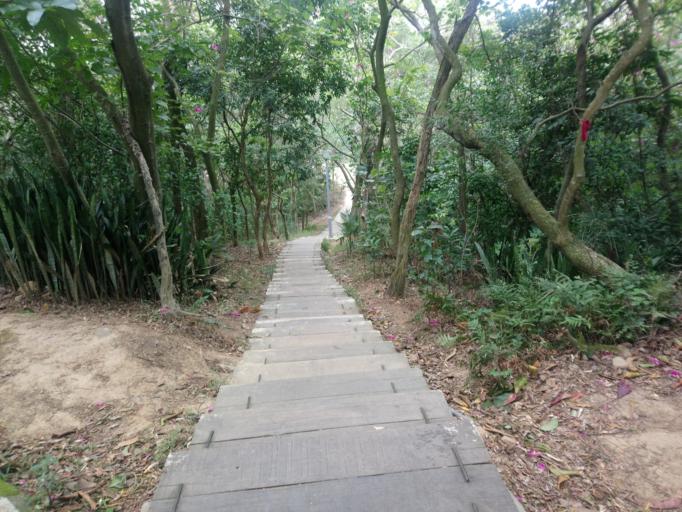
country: TW
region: Taiwan
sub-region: Hsinchu
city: Hsinchu
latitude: 24.7909
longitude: 120.9847
